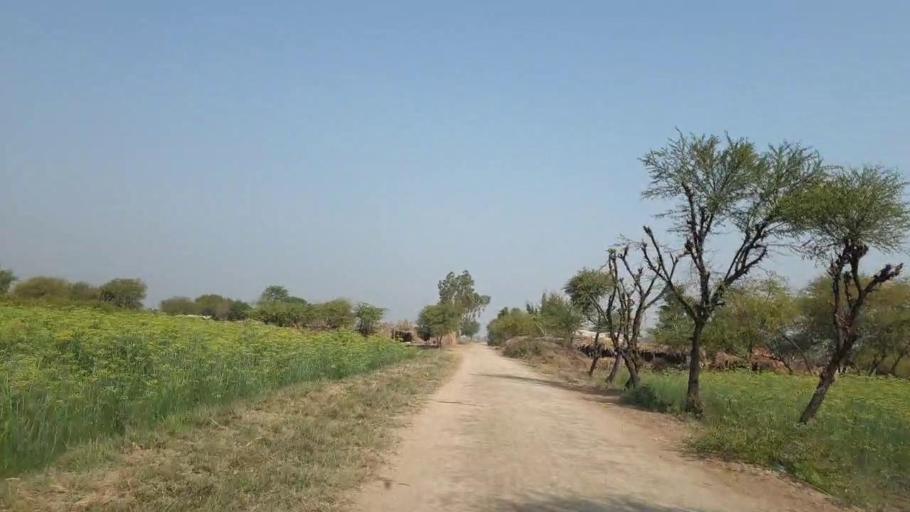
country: PK
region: Sindh
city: Mirpur Khas
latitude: 25.5892
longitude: 69.0149
